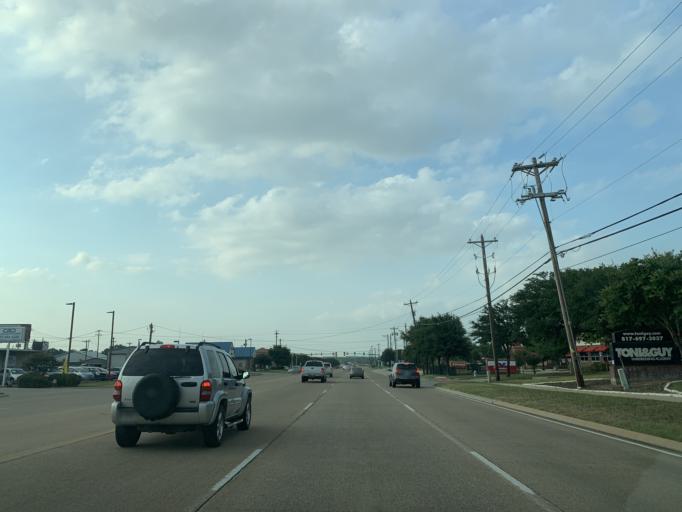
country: US
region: Texas
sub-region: Tarrant County
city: Keller
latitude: 32.9148
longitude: -97.2554
